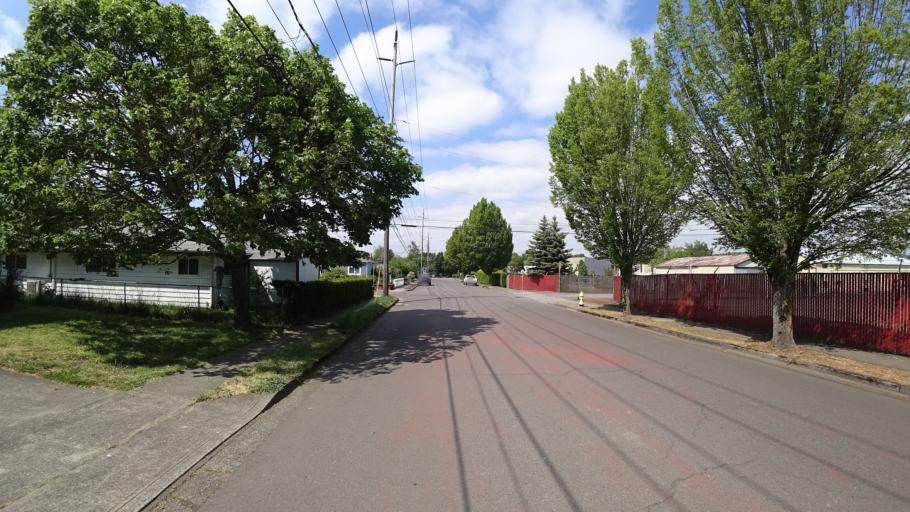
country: US
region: Oregon
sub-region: Washington County
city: Beaverton
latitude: 45.4815
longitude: -122.7966
